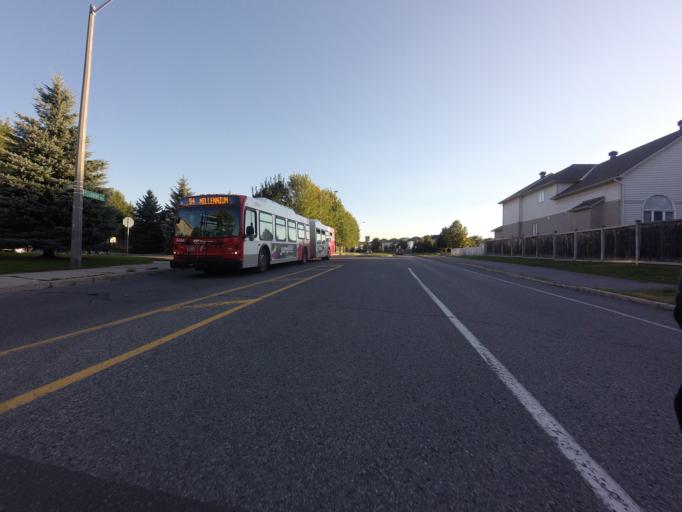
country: CA
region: Ontario
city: Ottawa
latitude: 45.2921
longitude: -75.7105
